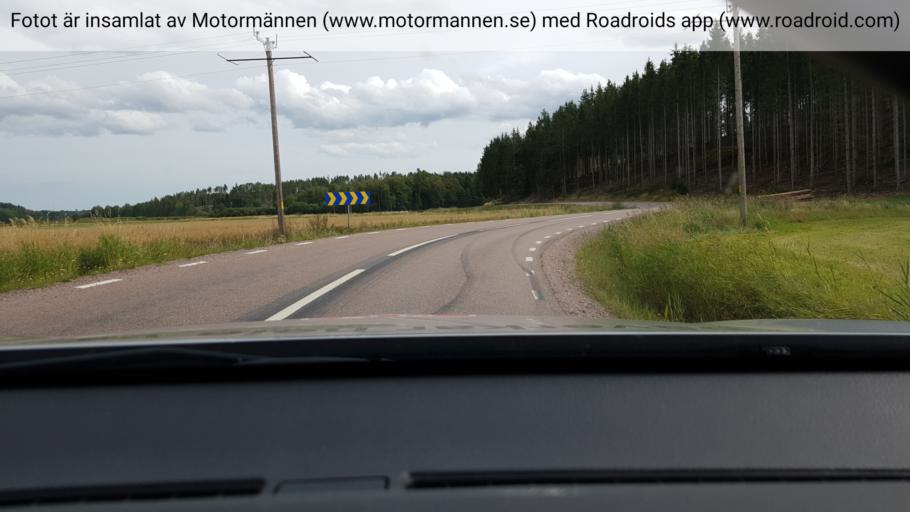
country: SE
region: Soedermanland
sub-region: Gnesta Kommun
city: Gnesta
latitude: 59.0462
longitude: 17.1581
